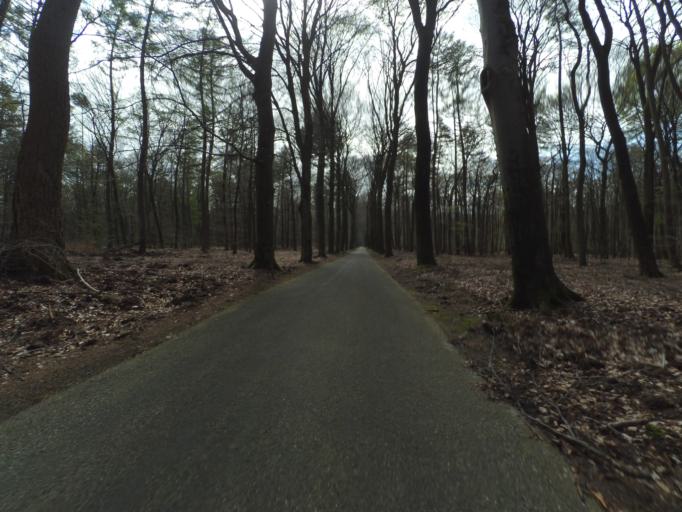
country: NL
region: Gelderland
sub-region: Gemeente Nunspeet
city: Nunspeet
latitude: 52.3545
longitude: 5.8553
